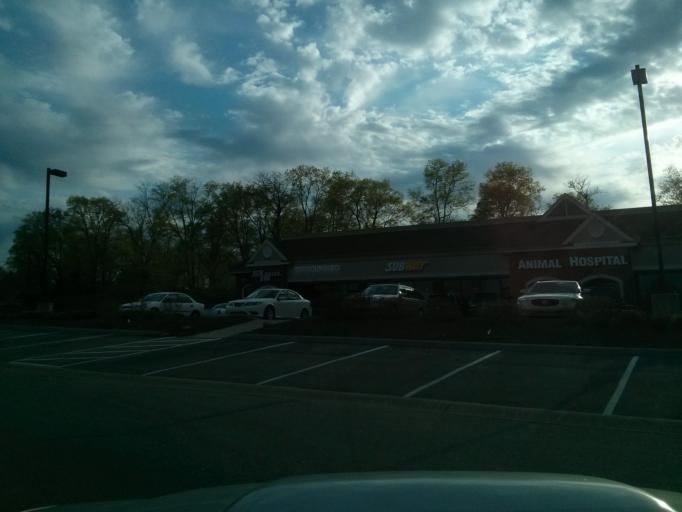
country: US
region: Indiana
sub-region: Hamilton County
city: Carmel
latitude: 39.9798
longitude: -86.0716
